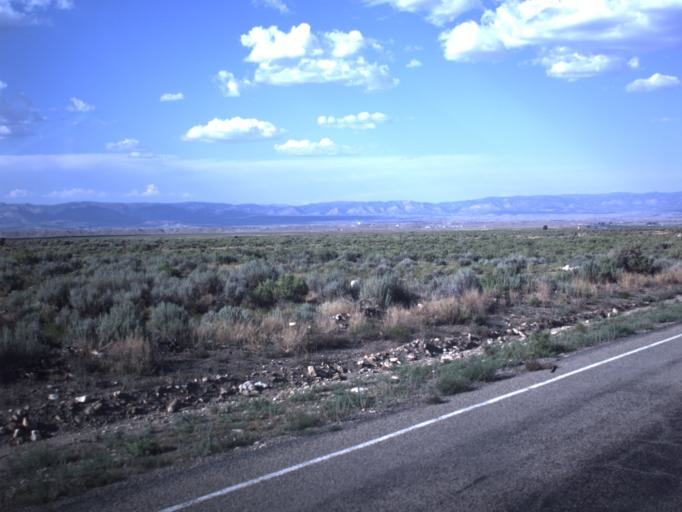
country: US
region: Utah
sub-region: Carbon County
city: Price
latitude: 39.4870
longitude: -110.8752
